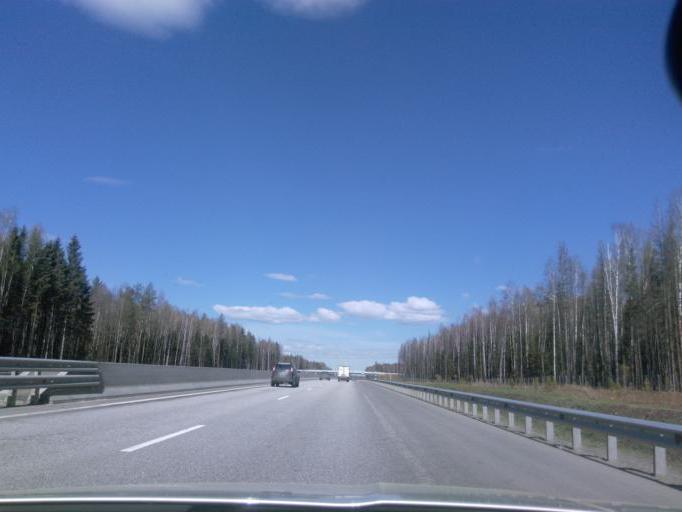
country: RU
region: Moskovskaya
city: Mendeleyevo
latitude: 56.0599
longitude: 37.2428
